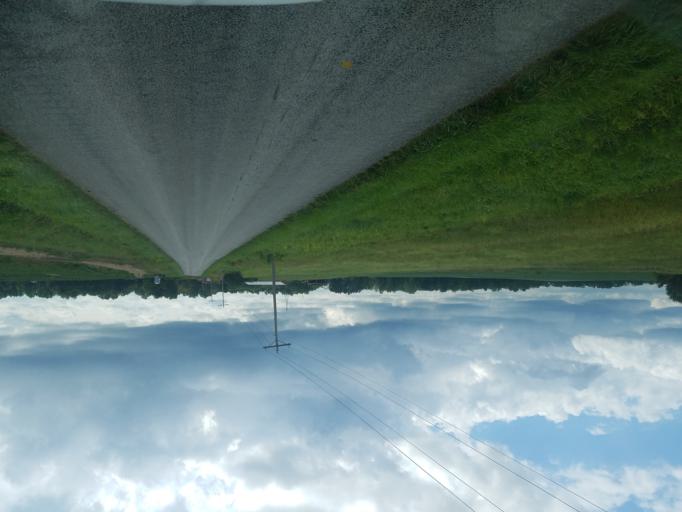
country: US
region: Ohio
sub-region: Huron County
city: Plymouth
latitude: 41.0832
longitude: -82.6290
